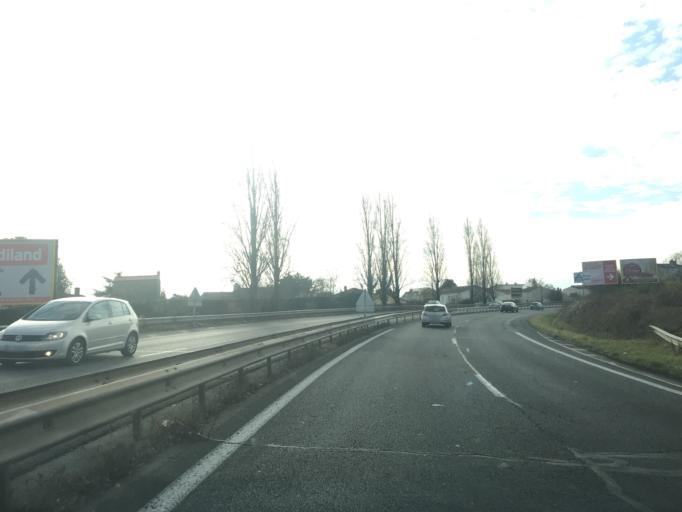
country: FR
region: Poitou-Charentes
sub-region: Departement des Deux-Sevres
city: Niort
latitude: 46.3341
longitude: -0.4658
